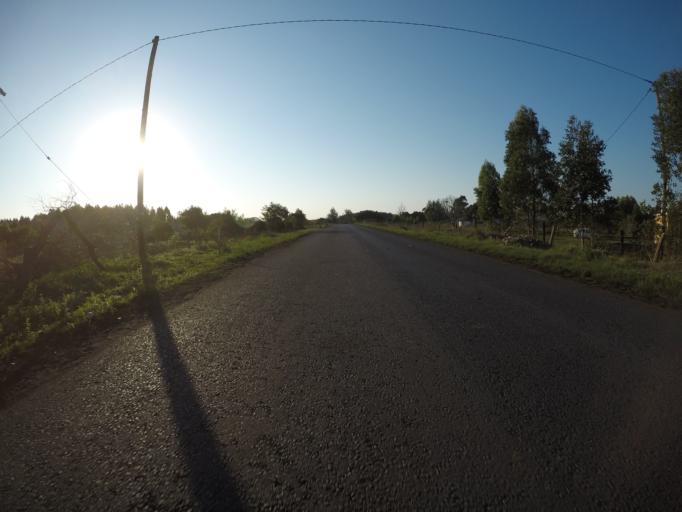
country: ZA
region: KwaZulu-Natal
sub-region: uThungulu District Municipality
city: KwaMbonambi
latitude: -28.6864
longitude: 32.2065
